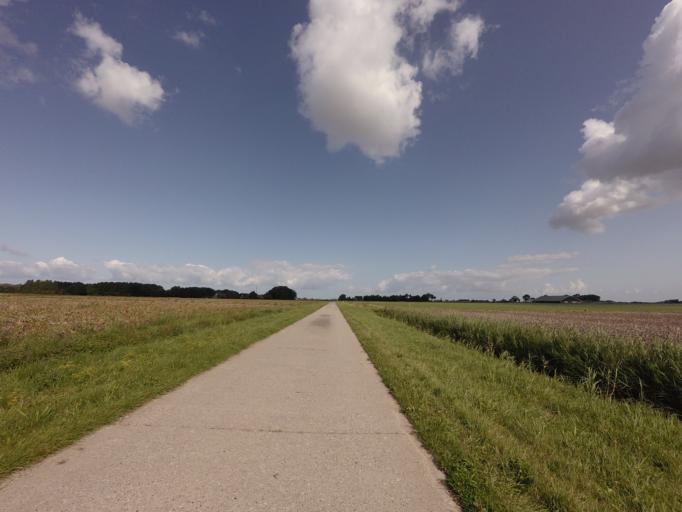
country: NL
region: Friesland
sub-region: Gemeente Het Bildt
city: Sint Jacobiparochie
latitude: 53.2684
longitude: 5.6163
